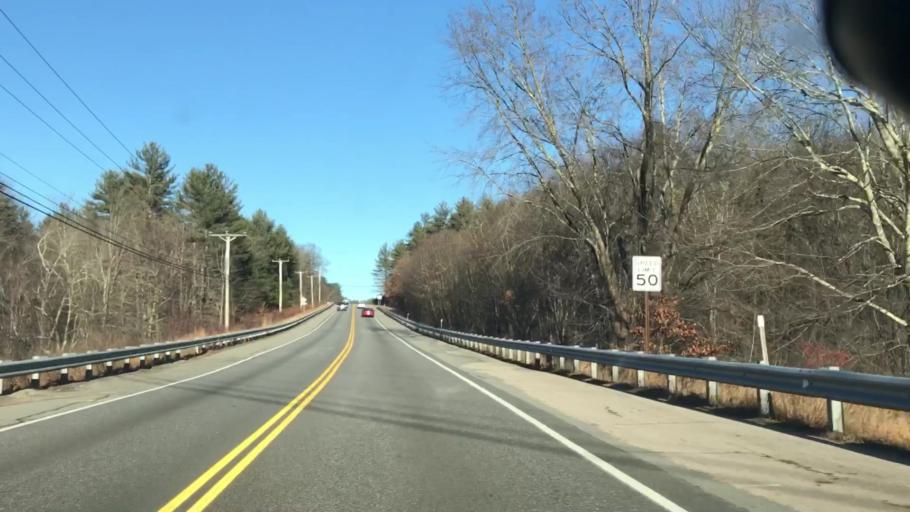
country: US
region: New Hampshire
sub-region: Hillsborough County
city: Bedford
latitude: 42.9058
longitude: -71.5699
